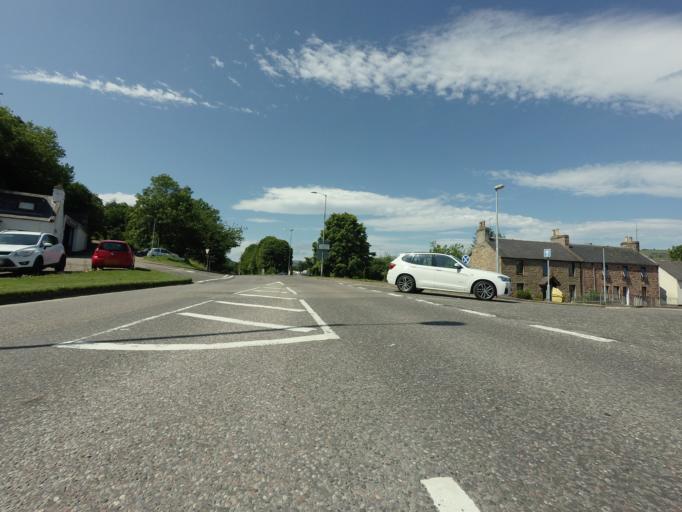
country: GB
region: Scotland
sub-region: Highland
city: Dingwall
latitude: 57.5937
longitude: -4.4262
